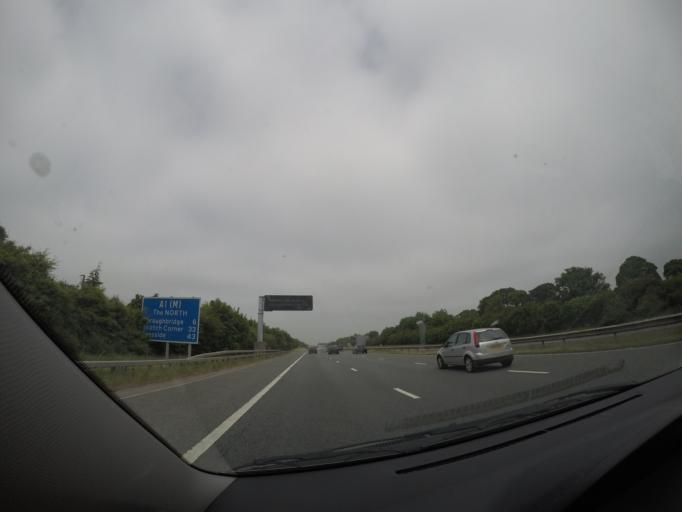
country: GB
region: England
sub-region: North Yorkshire
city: Boroughbridge
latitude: 54.0163
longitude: -1.3811
